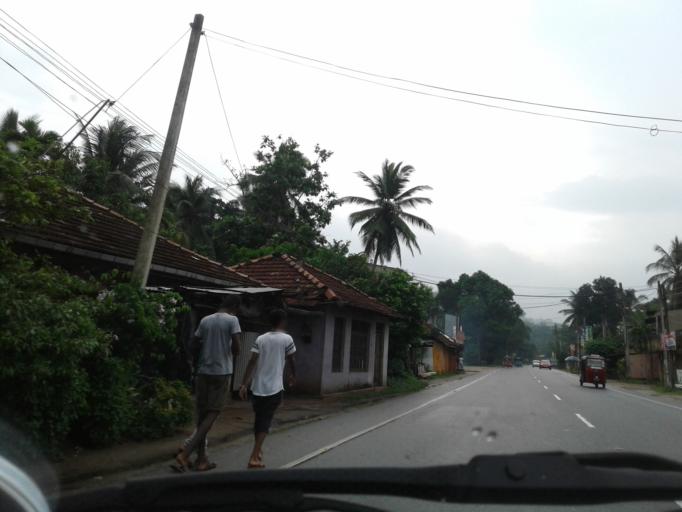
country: LK
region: Central
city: Kadugannawa
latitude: 7.2370
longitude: 80.2950
